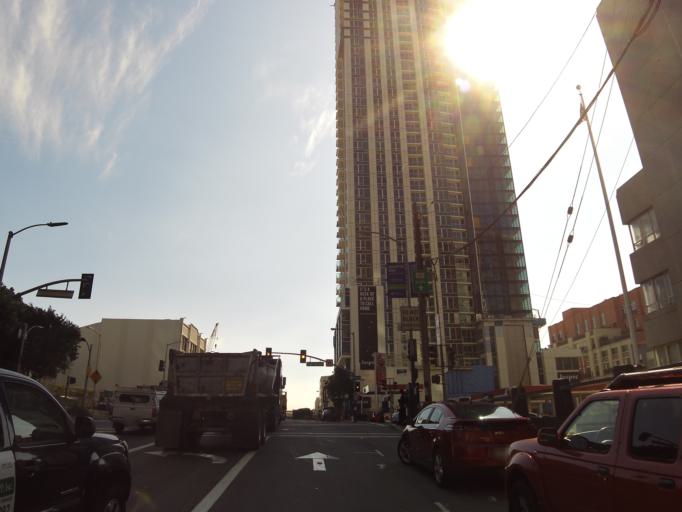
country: US
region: California
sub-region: San Francisco County
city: San Francisco
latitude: 37.7864
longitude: -122.3927
